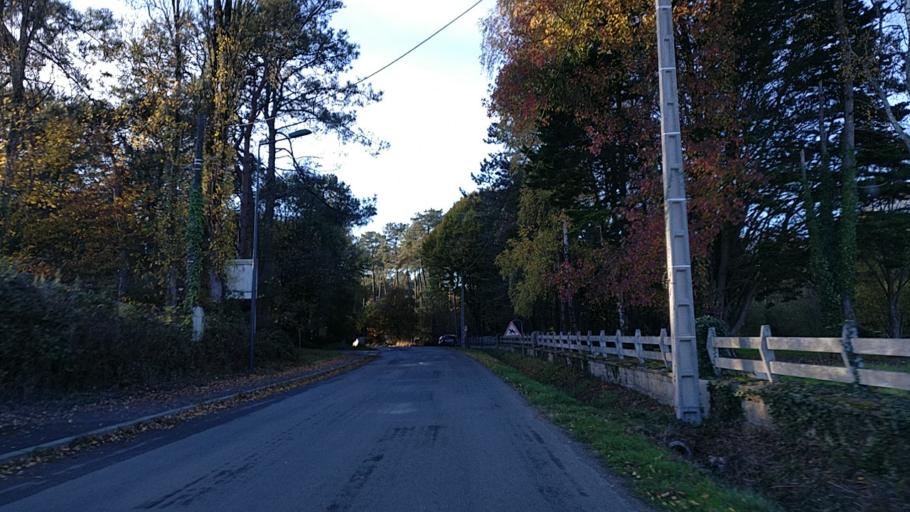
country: FR
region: Brittany
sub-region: Departement d'Ille-et-Vilaine
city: Liffre
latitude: 48.1891
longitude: -1.5232
